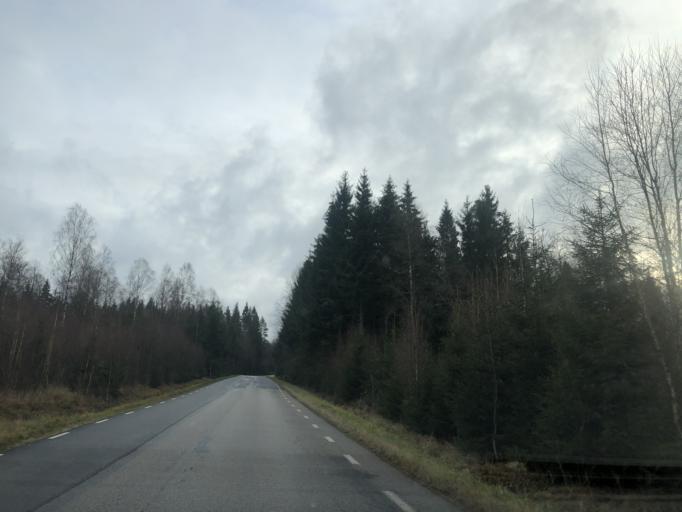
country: SE
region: Vaestra Goetaland
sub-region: Boras Kommun
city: Dalsjofors
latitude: 57.8155
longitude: 13.1976
